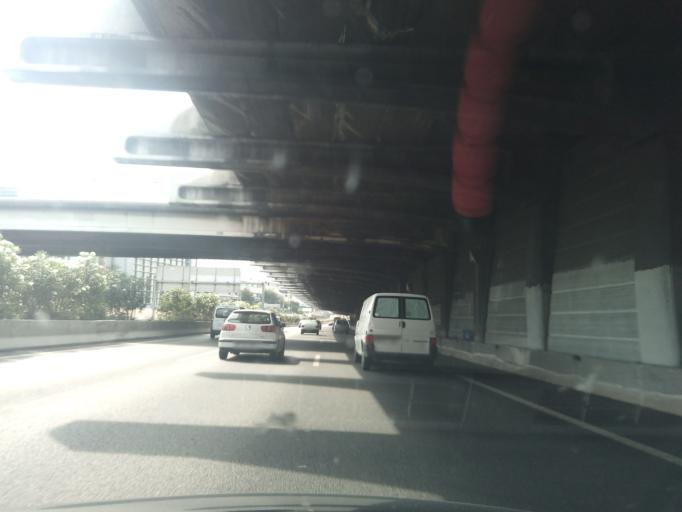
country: ES
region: Madrid
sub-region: Provincia de Madrid
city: Hortaleza
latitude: 40.4741
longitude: -3.6343
